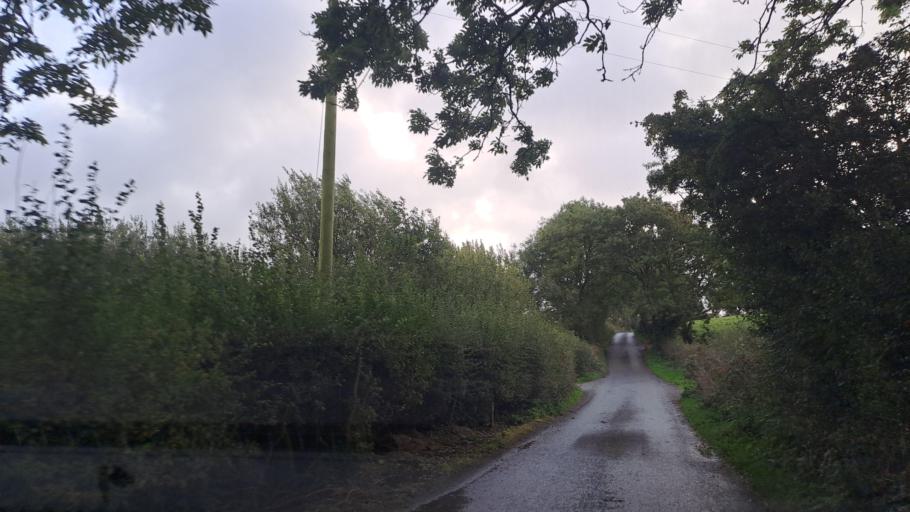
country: IE
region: Ulster
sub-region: An Cabhan
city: Kingscourt
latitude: 53.9648
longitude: -6.8304
